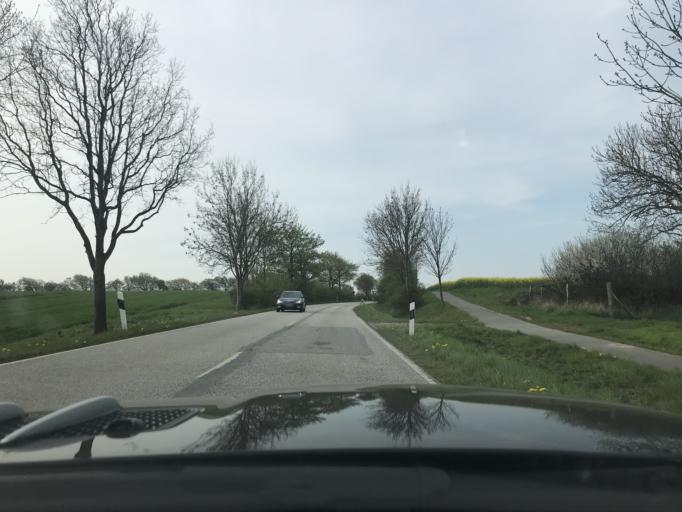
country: DE
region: Schleswig-Holstein
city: Neukirchen
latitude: 54.3117
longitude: 11.0130
